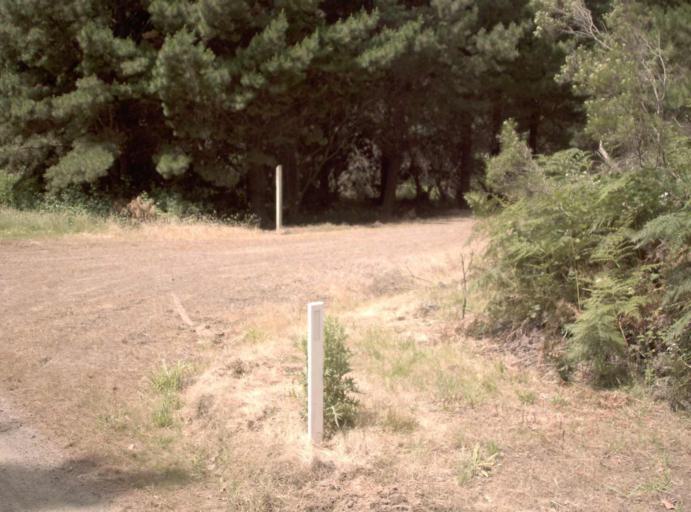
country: AU
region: Victoria
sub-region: Latrobe
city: Traralgon
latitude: -38.3831
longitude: 146.6652
